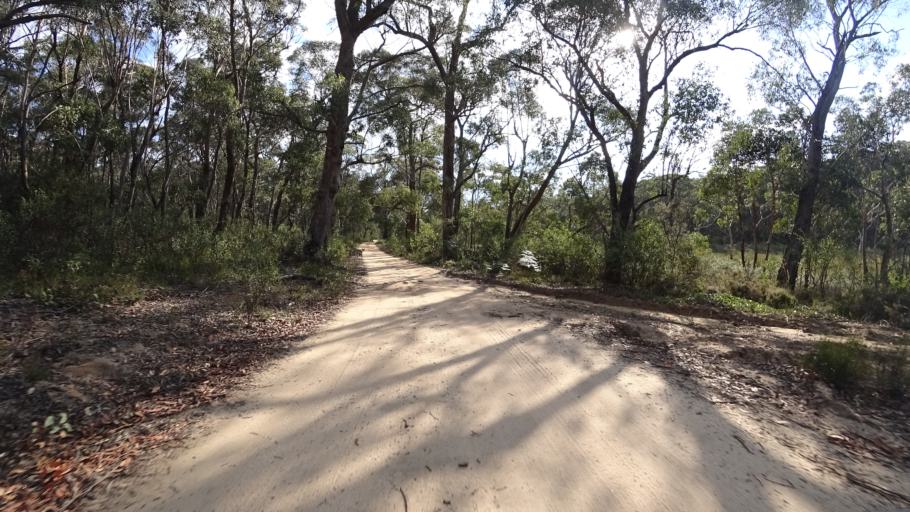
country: AU
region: New South Wales
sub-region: Lithgow
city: Lithgow
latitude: -33.3381
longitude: 150.2738
